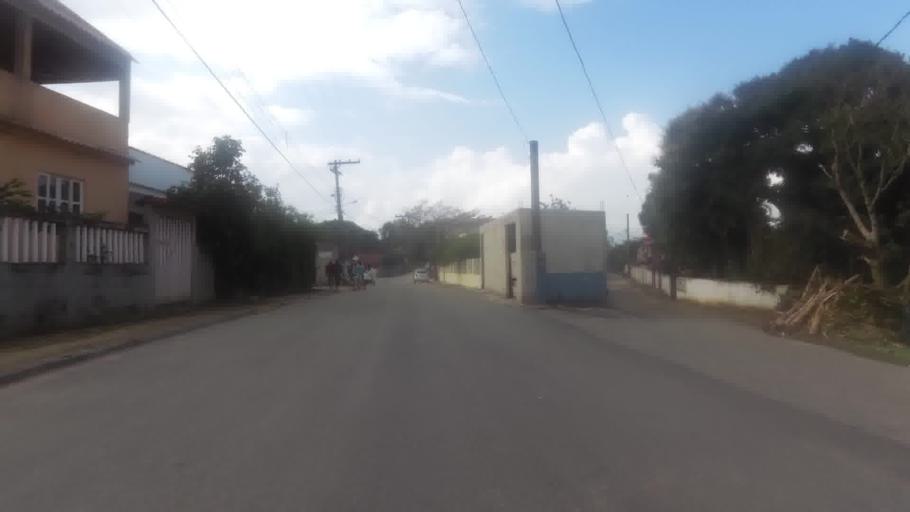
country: BR
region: Espirito Santo
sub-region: Guarapari
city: Guarapari
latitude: -20.7648
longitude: -40.5756
